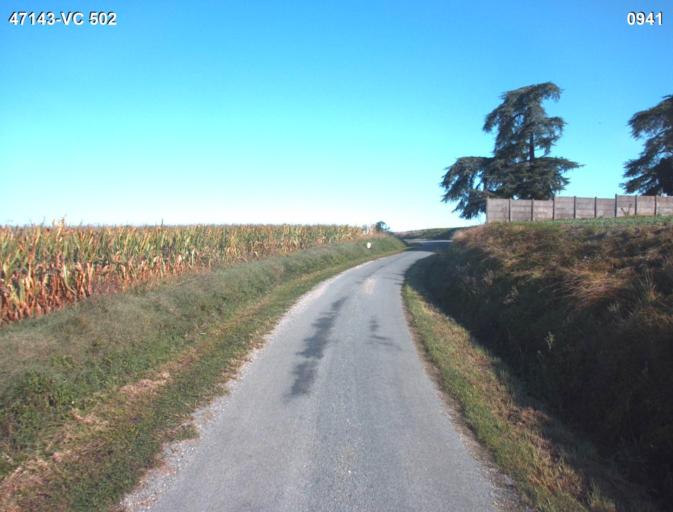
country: FR
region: Aquitaine
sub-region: Departement du Lot-et-Garonne
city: Vianne
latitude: 44.1720
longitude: 0.3271
